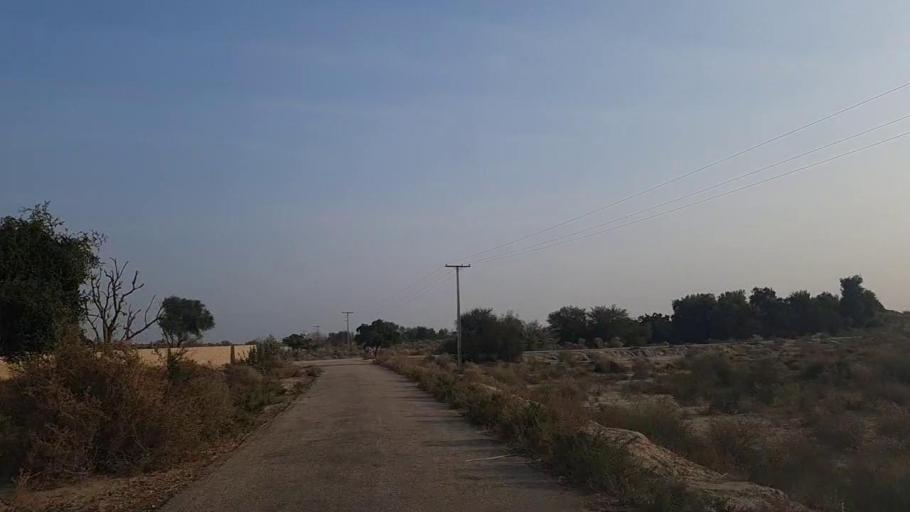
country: PK
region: Sindh
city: Jam Sahib
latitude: 26.4336
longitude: 68.5934
